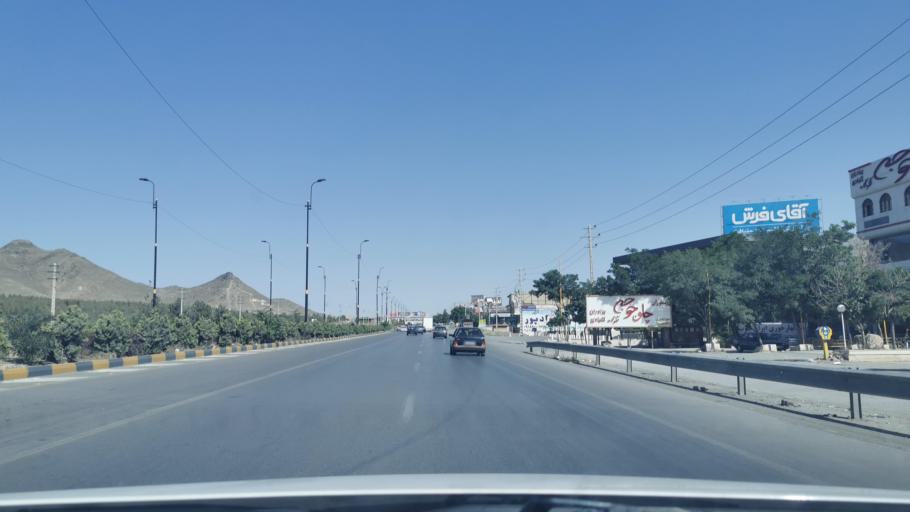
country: IR
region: Razavi Khorasan
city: Torqabeh
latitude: 36.3897
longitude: 59.4066
